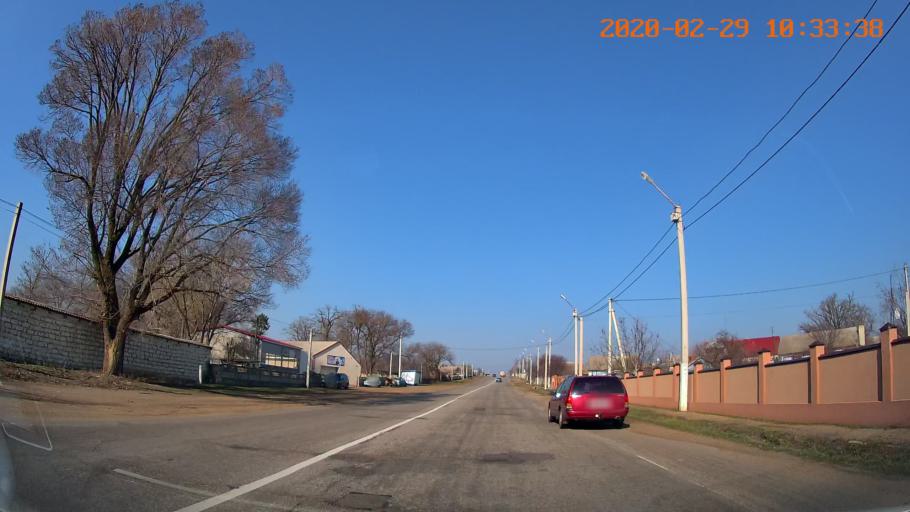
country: MD
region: Anenii Noi
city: Varnita
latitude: 46.9714
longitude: 29.5425
